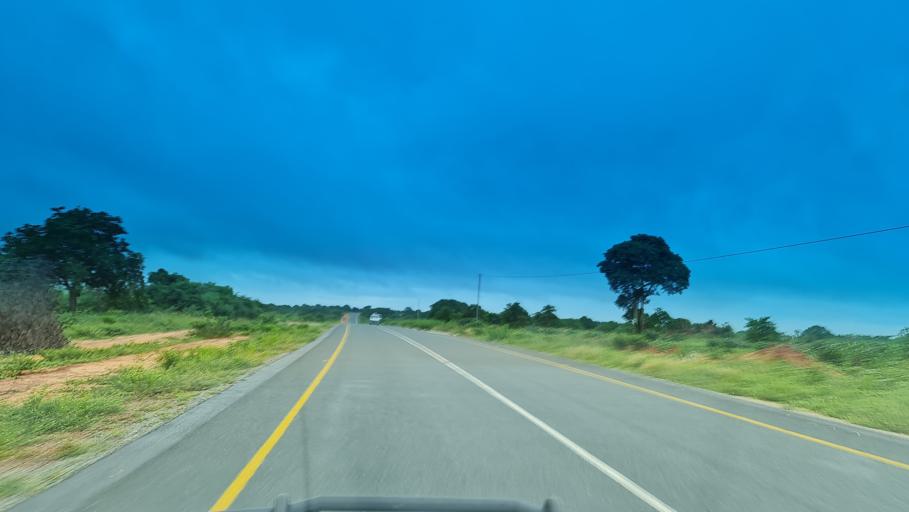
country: MZ
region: Nampula
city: Nampula
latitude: -15.6072
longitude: 39.3285
